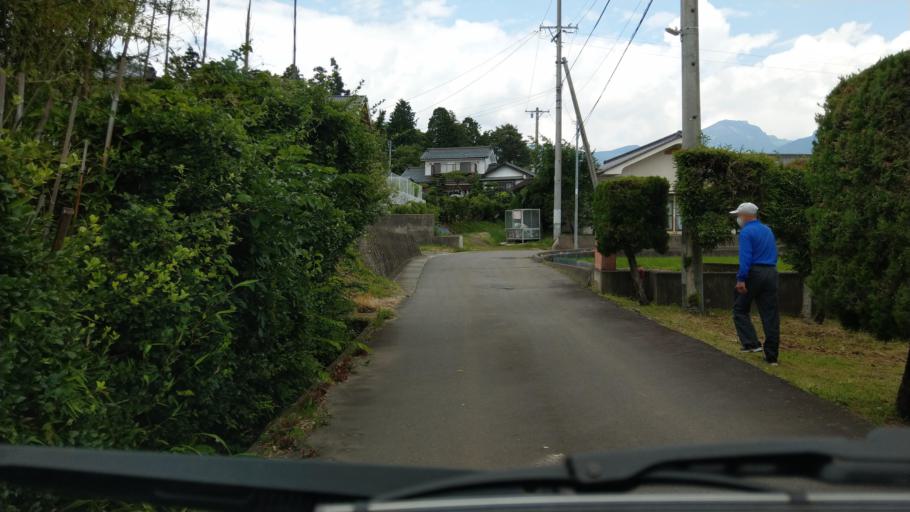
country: JP
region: Nagano
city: Komoro
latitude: 36.3226
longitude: 138.4512
